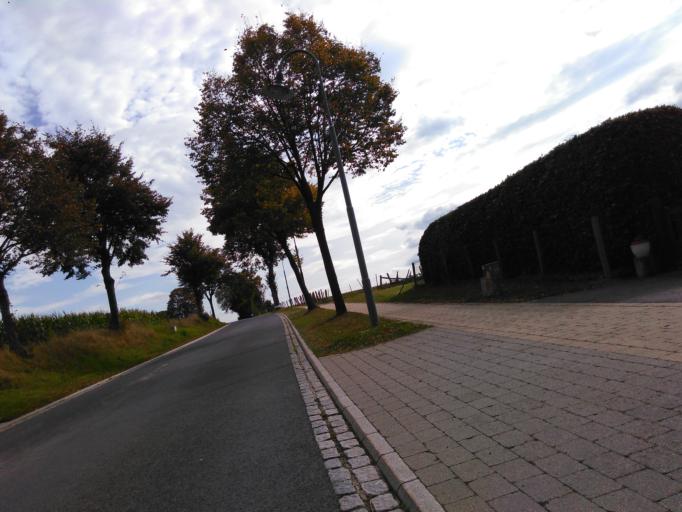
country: LU
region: Diekirch
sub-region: Canton de Clervaux
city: Troisvierges
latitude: 50.1402
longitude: 5.9845
